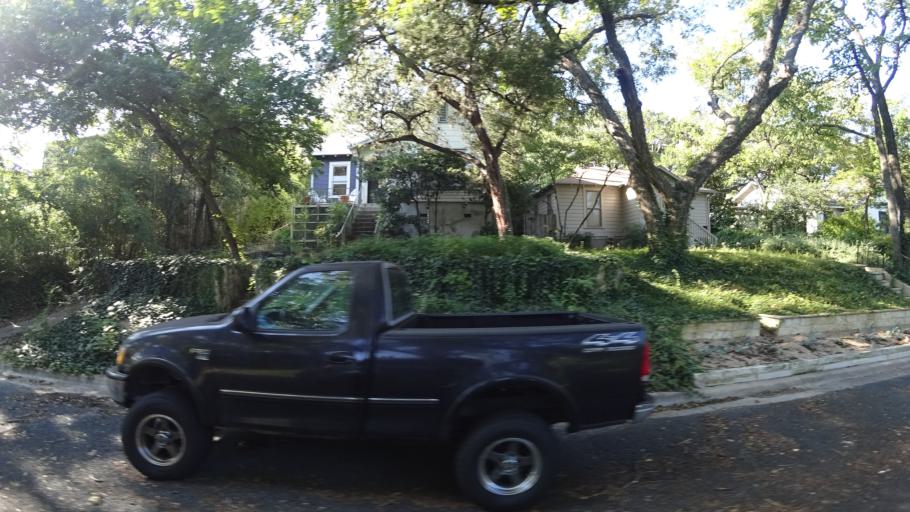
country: US
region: Texas
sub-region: Travis County
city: Austin
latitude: 30.2497
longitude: -97.7410
